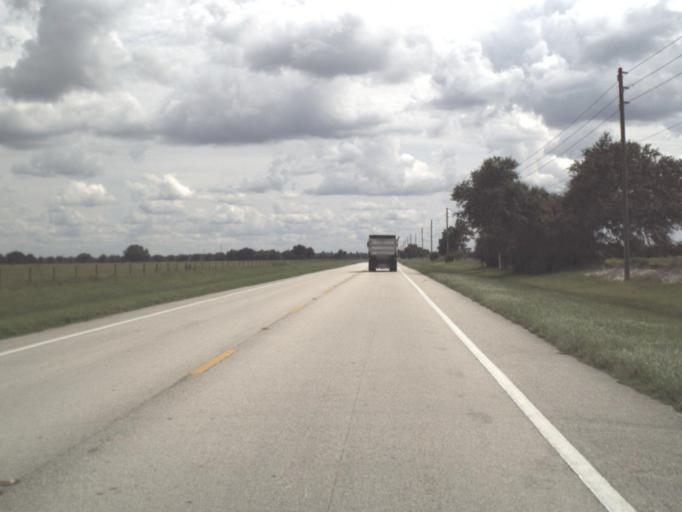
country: US
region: Florida
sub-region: DeSoto County
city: Nocatee
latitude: 27.0398
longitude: -81.7759
